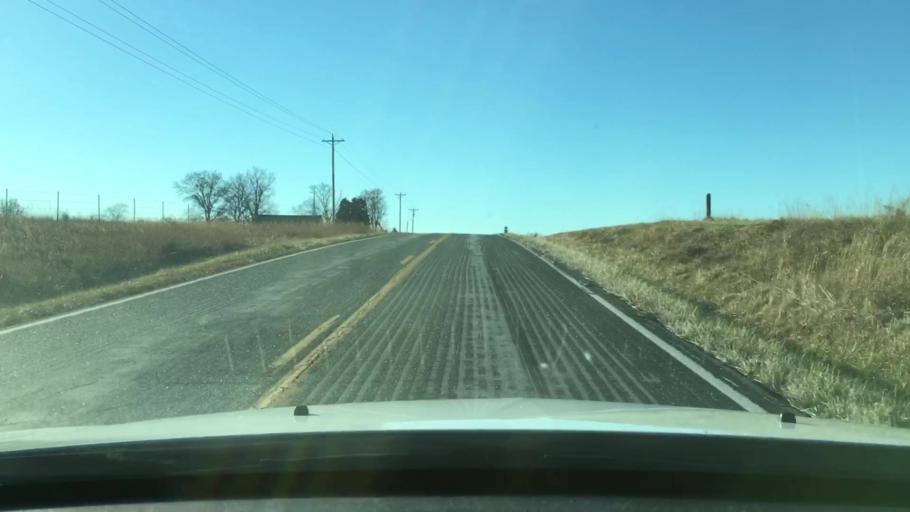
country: US
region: Missouri
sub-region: Audrain County
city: Mexico
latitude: 39.2805
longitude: -91.7653
